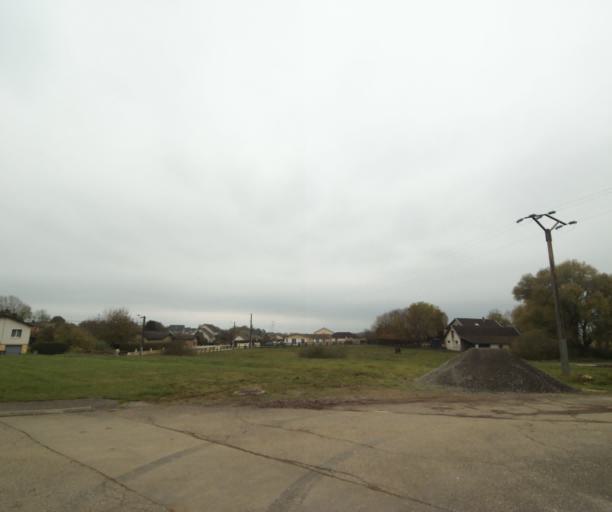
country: FR
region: Lorraine
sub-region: Departement de Meurthe-et-Moselle
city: Briey
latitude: 49.2516
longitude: 5.9093
